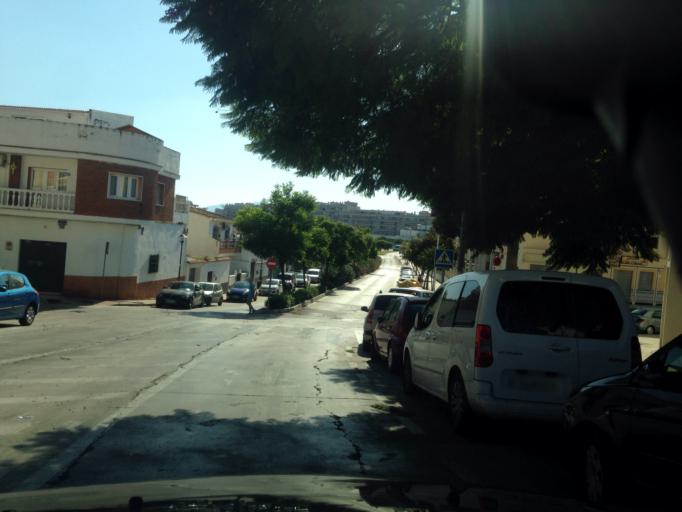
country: ES
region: Andalusia
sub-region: Provincia de Malaga
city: Malaga
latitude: 36.7233
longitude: -4.4572
